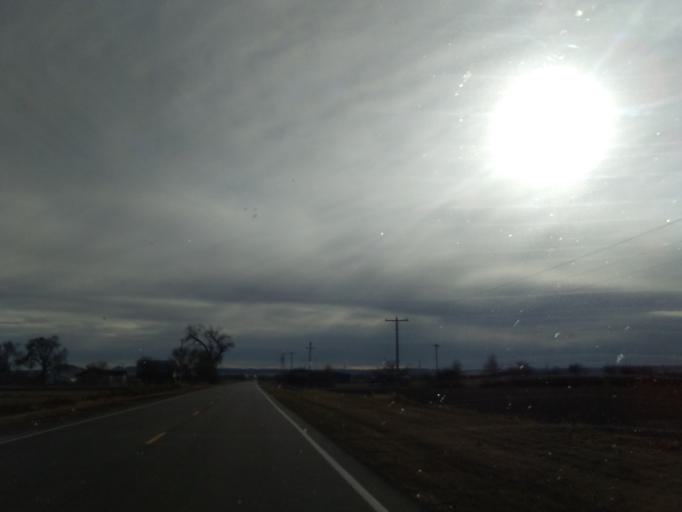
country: US
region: Nebraska
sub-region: Scotts Bluff County
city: Gering
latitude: 41.8094
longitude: -103.5193
